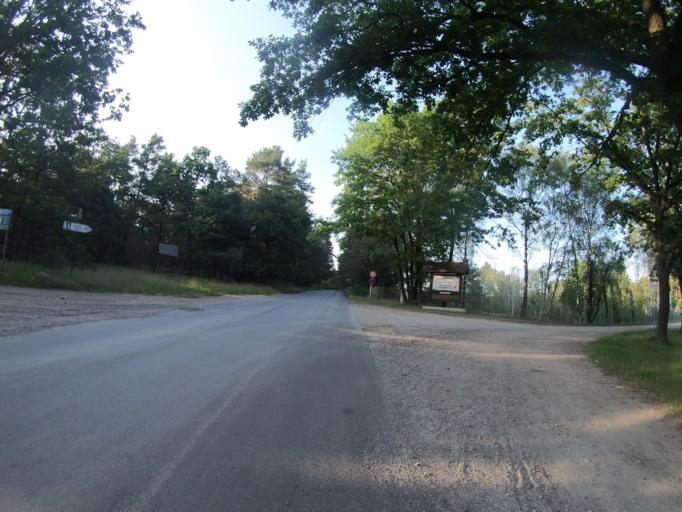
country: DE
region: Lower Saxony
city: Wagenhoff
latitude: 52.5222
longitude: 10.4789
